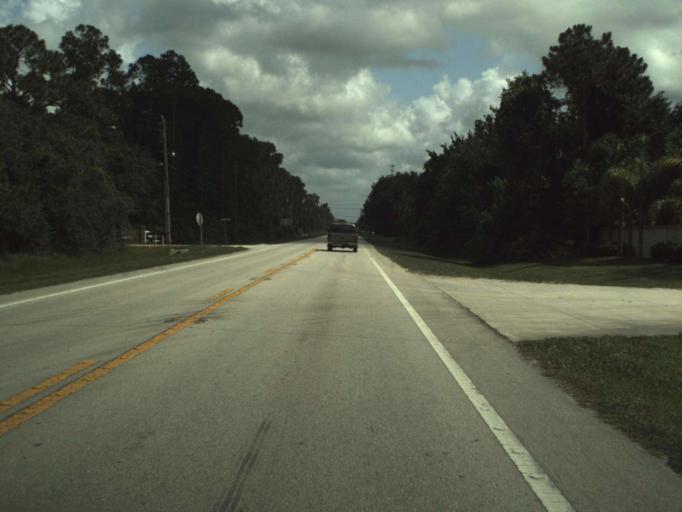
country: US
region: Florida
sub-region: Volusia County
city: Samsula-Spruce Creek
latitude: 28.9995
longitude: -81.0707
